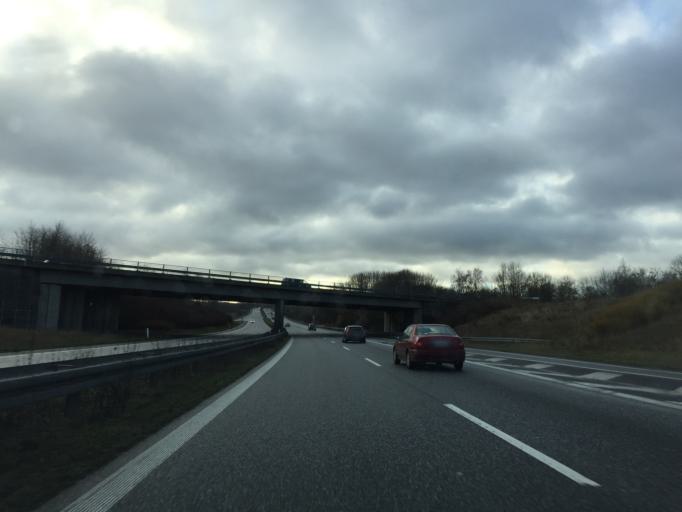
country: DK
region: Zealand
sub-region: Slagelse Kommune
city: Slagelse
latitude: 55.4192
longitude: 11.4146
